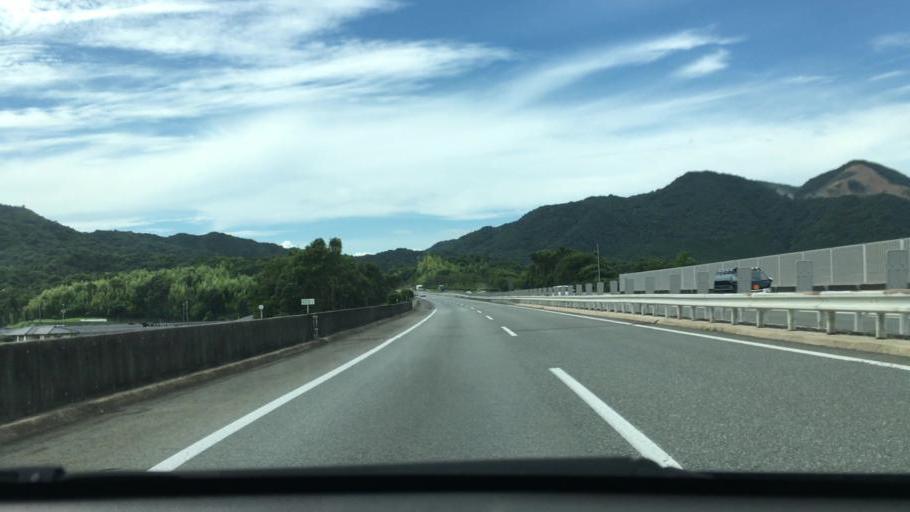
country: JP
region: Yamaguchi
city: Hofu
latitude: 34.0709
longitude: 131.4975
